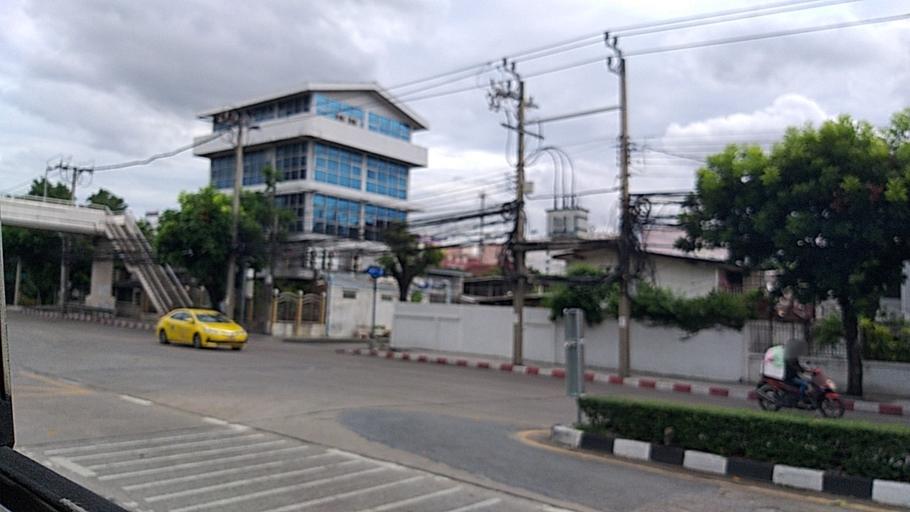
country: TH
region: Bangkok
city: Bang Kapi
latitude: 13.7763
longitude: 100.6451
